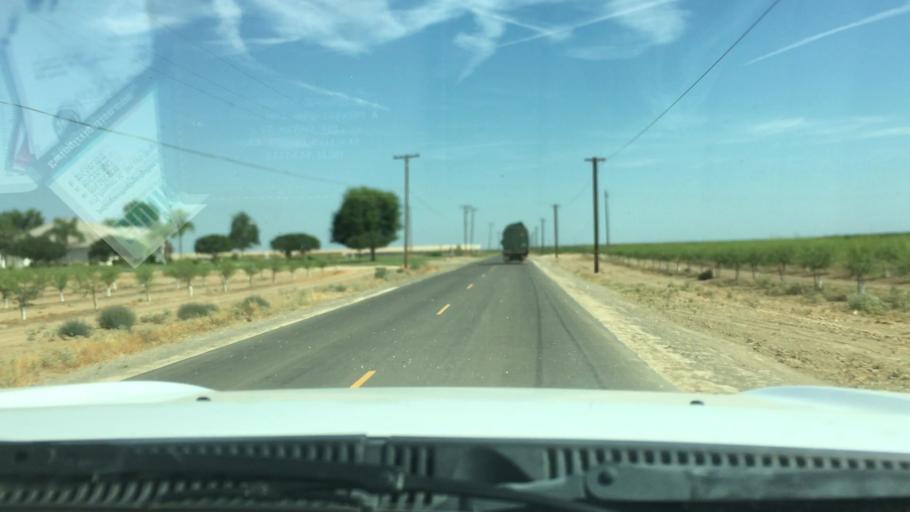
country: US
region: California
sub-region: Kern County
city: Shafter
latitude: 35.4623
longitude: -119.3681
